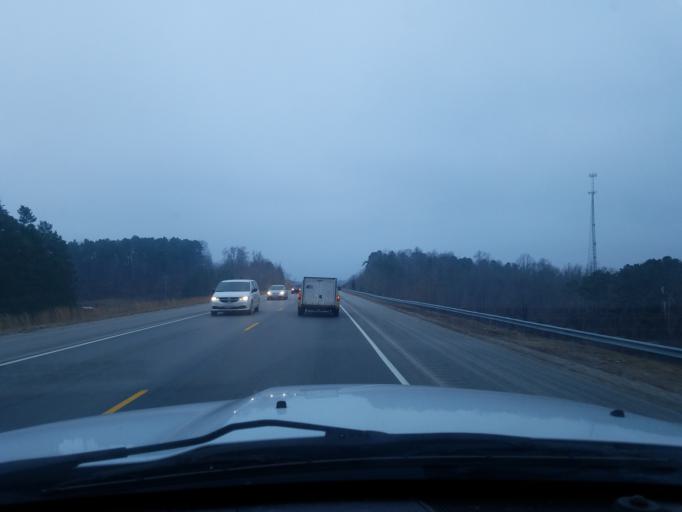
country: US
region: Indiana
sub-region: Perry County
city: Tell City
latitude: 38.0694
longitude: -86.6187
